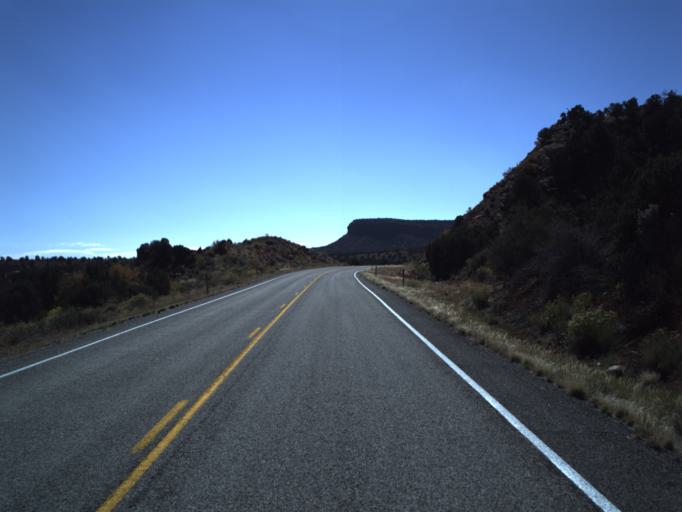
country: US
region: Utah
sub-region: San Juan County
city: Blanding
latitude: 37.5877
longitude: -110.0405
